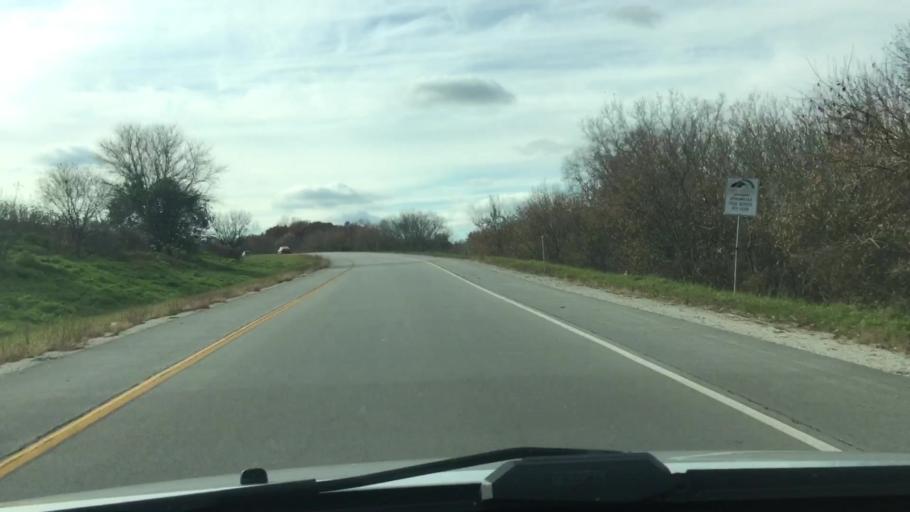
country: US
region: Wisconsin
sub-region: Waukesha County
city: Hartland
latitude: 43.1102
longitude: -88.3468
